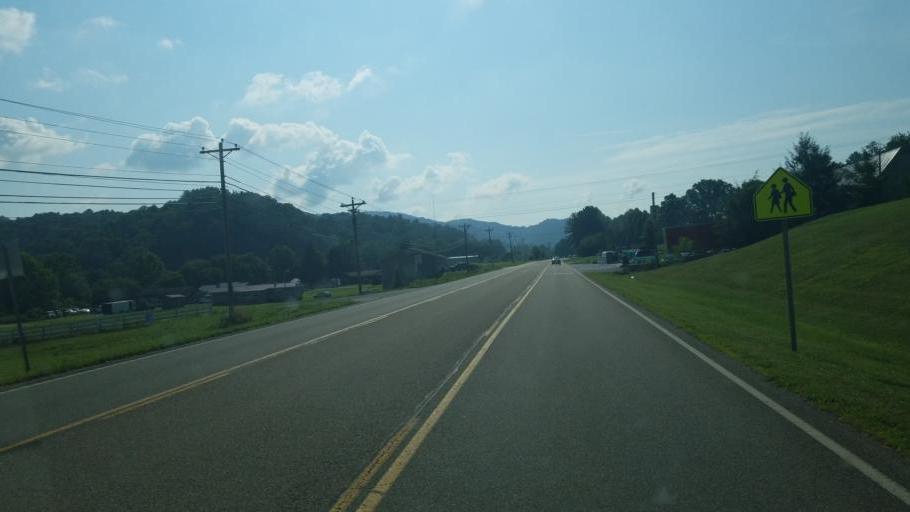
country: US
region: Tennessee
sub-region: Carter County
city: Roan Mountain
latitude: 36.1937
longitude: -82.0567
